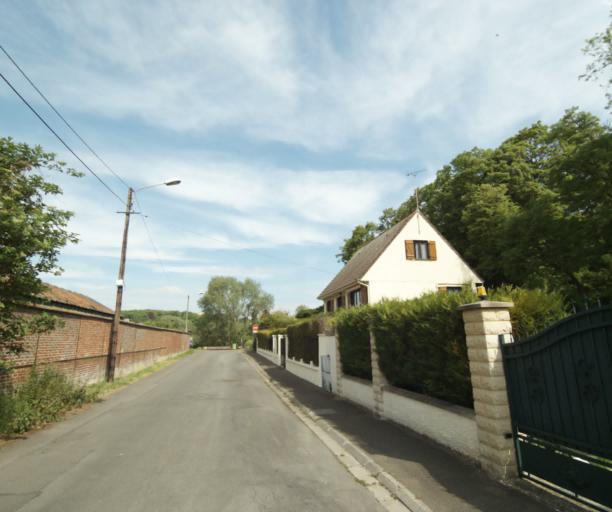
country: FR
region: Ile-de-France
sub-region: Departement des Yvelines
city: Les Mureaux
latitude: 48.9968
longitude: 1.9009
